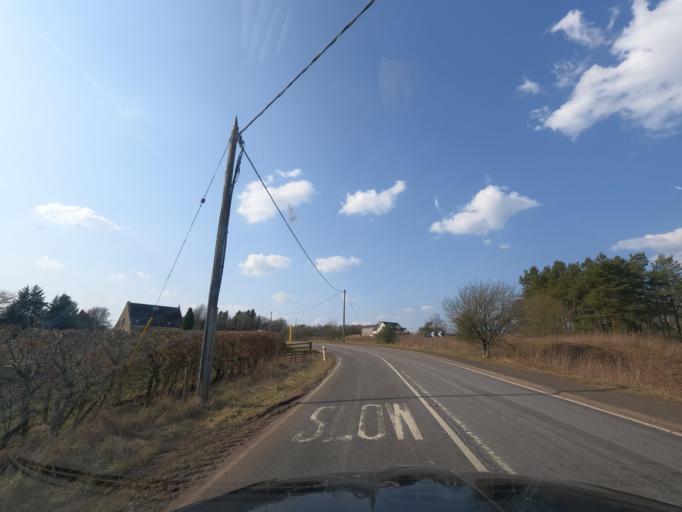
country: GB
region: Scotland
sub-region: South Lanarkshire
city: Forth
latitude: 55.7729
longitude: -3.6736
